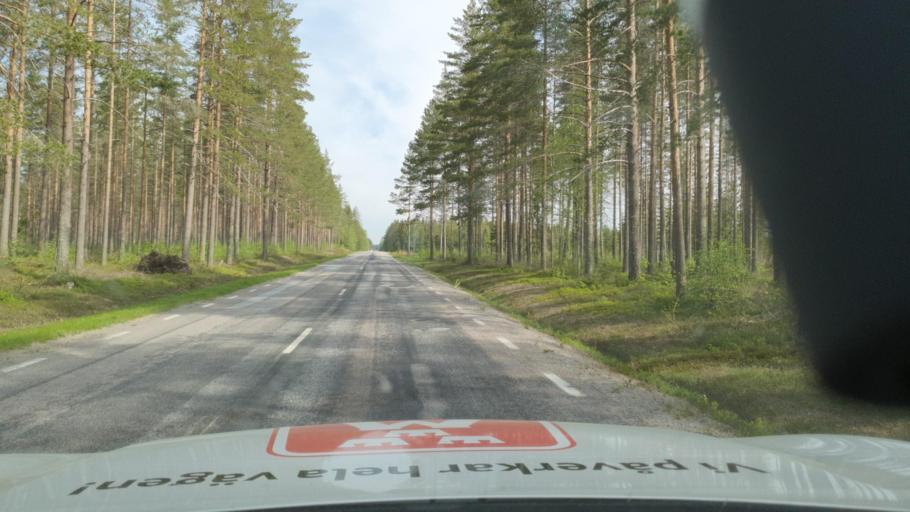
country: SE
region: Vaesterbotten
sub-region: Umea Kommun
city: Hoernefors
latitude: 63.6855
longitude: 19.9193
